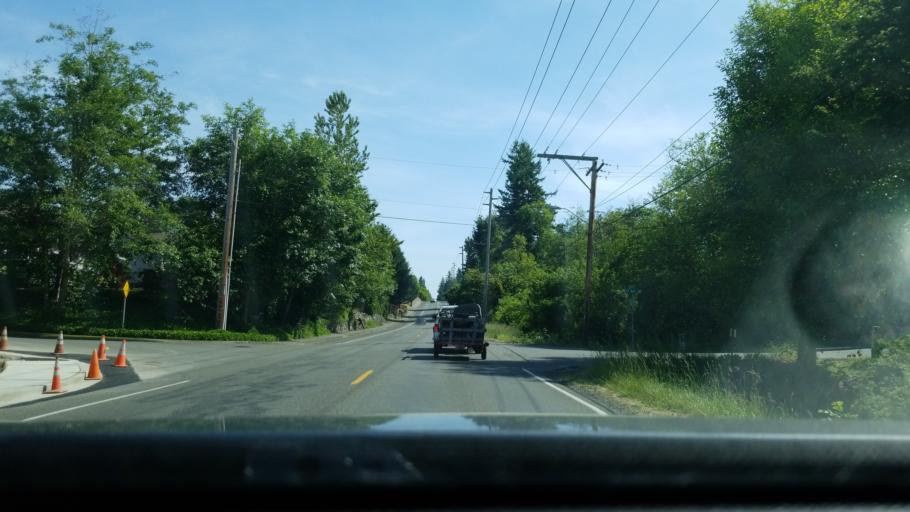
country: US
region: Washington
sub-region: Pierce County
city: Puyallup
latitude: 47.1738
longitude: -122.3043
